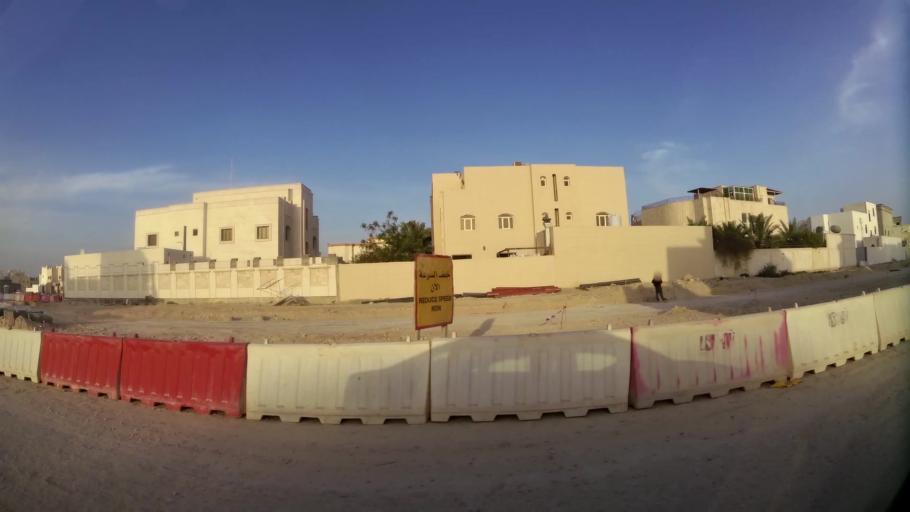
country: QA
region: Al Wakrah
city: Al Wakrah
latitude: 25.1449
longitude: 51.5952
